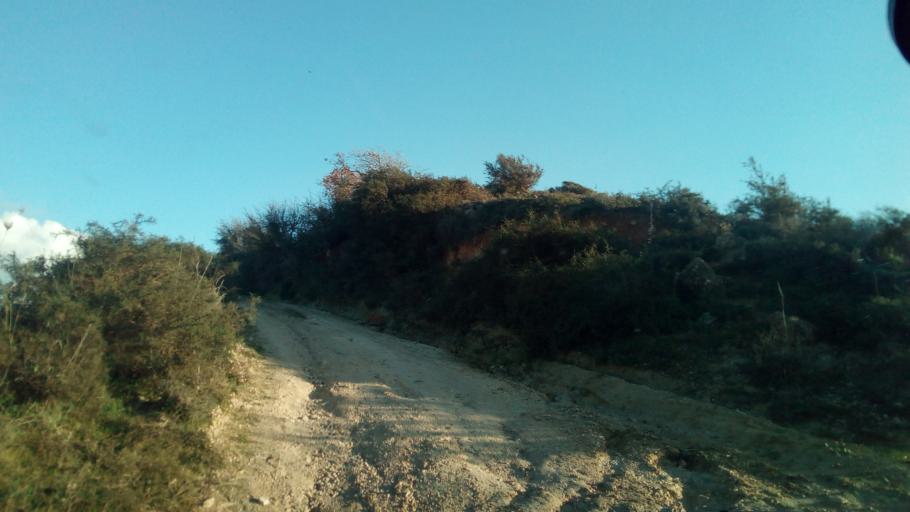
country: CY
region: Pafos
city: Mesogi
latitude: 34.8465
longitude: 32.4862
